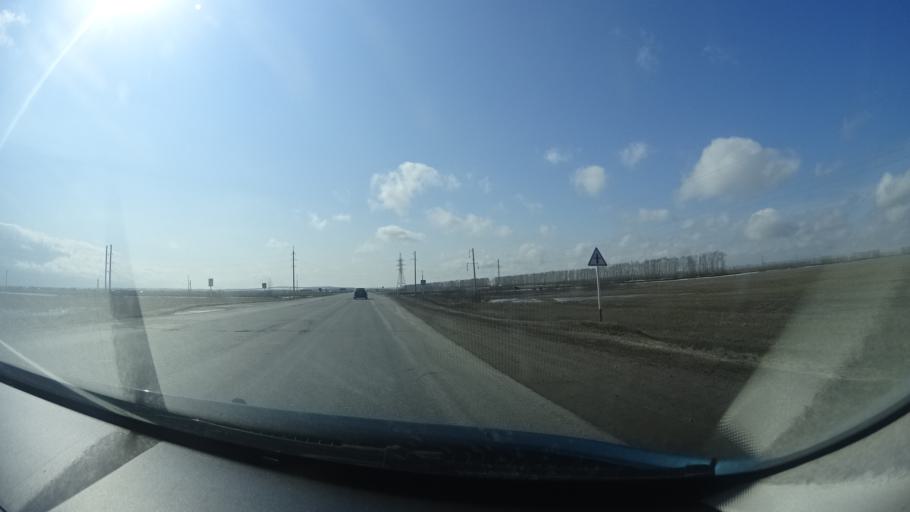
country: RU
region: Bashkortostan
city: Mikhaylovka
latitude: 54.9505
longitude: 55.7534
